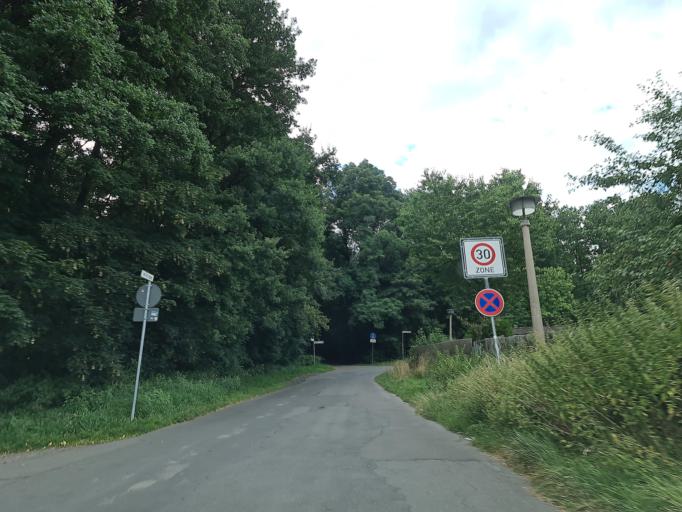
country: DE
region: Saxony
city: Plauen
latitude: 50.5201
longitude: 12.1221
